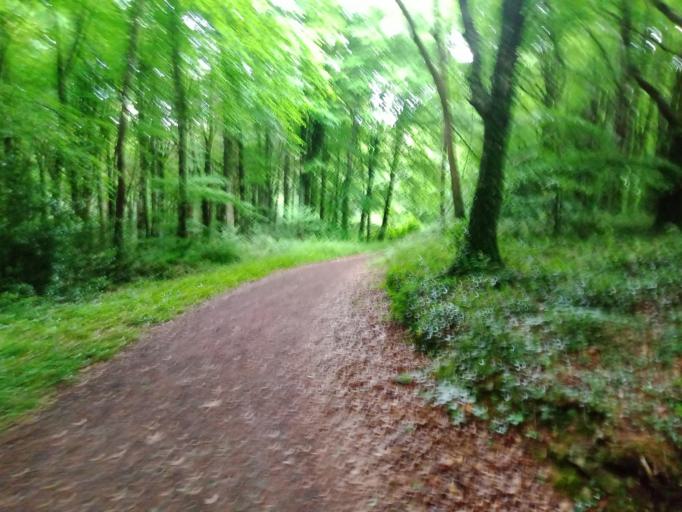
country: IE
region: Leinster
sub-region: Laois
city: Stradbally
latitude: 53.0016
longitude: -7.1227
